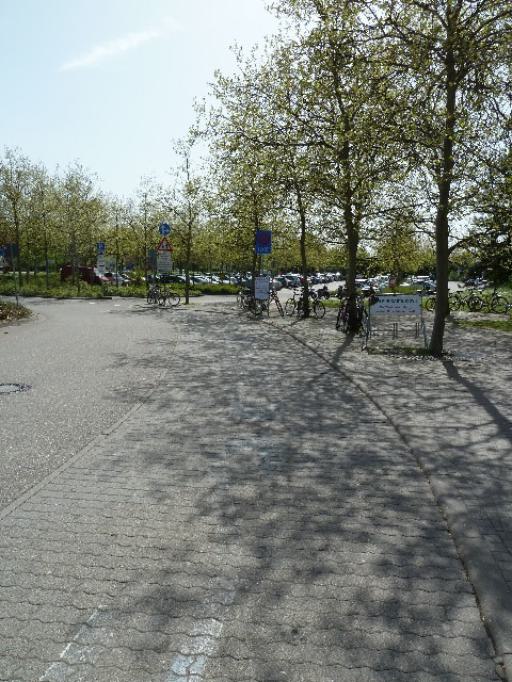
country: DE
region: Baden-Wuerttemberg
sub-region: Karlsruhe Region
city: Hockenheim
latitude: 49.3169
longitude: 8.5379
